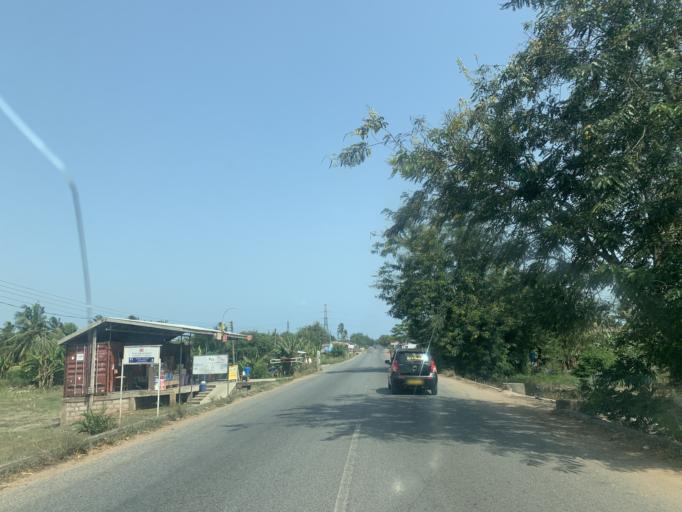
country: GH
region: Central
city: Winneba
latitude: 5.3915
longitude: -0.6465
